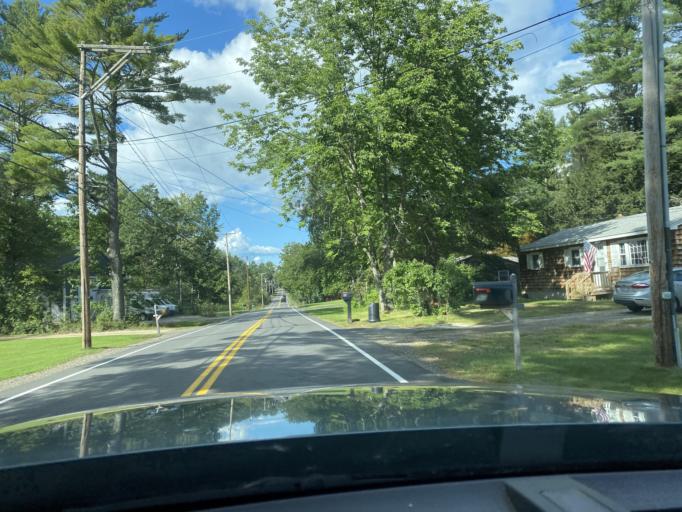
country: US
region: Maine
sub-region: York County
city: Kittery
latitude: 43.1502
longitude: -70.7123
